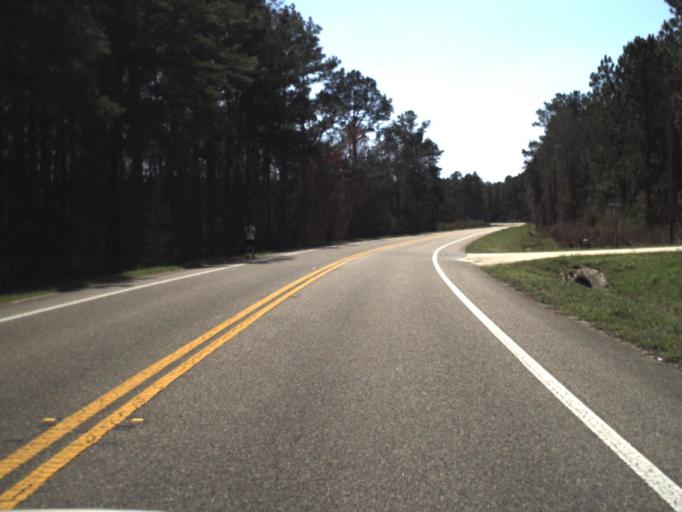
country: US
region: Florida
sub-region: Calhoun County
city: Blountstown
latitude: 30.5513
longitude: -85.0223
